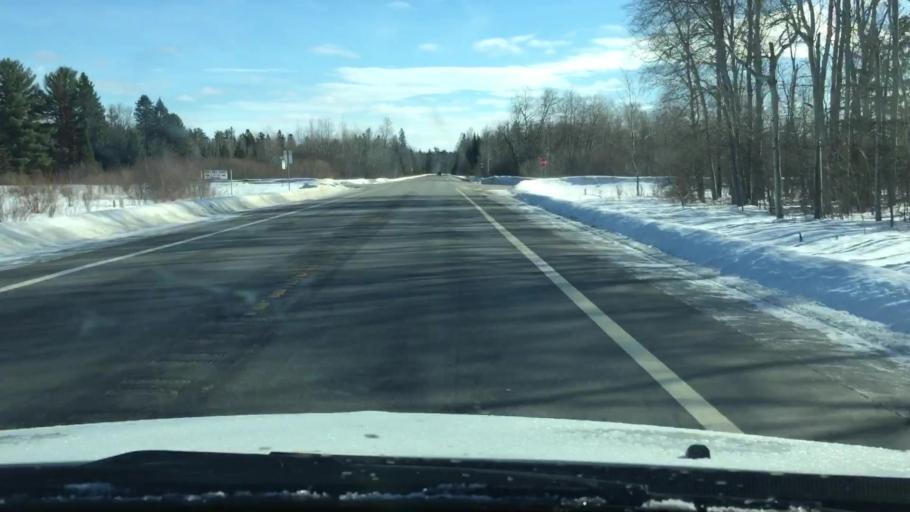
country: US
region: Michigan
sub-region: Charlevoix County
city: East Jordan
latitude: 45.0611
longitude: -85.0784
